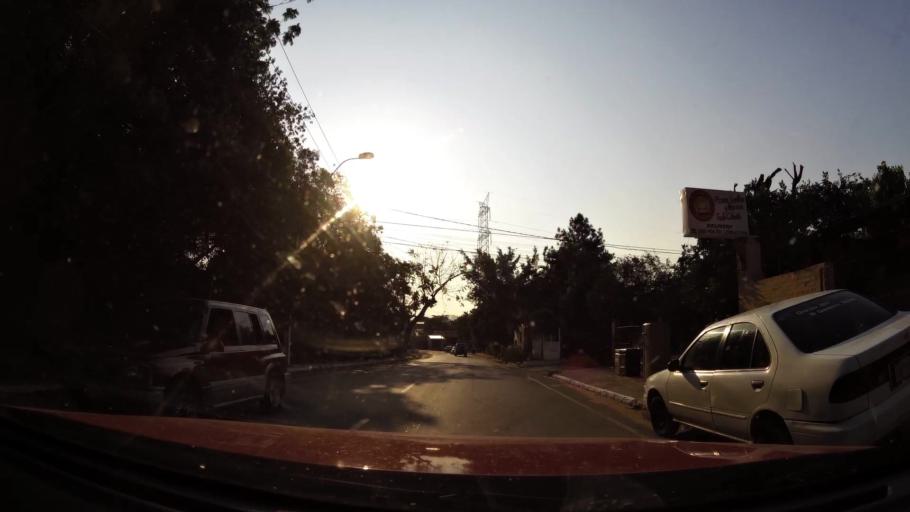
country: PY
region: Central
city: Lambare
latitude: -25.3553
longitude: -57.6077
